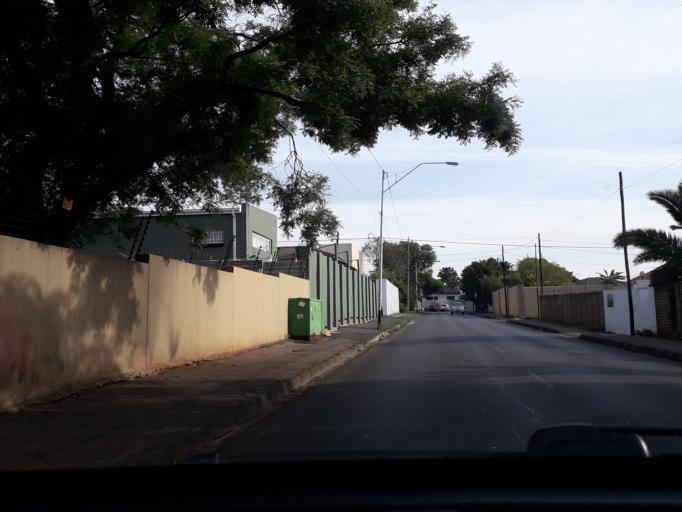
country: ZA
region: Gauteng
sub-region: City of Johannesburg Metropolitan Municipality
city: Johannesburg
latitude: -26.1504
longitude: 28.0970
